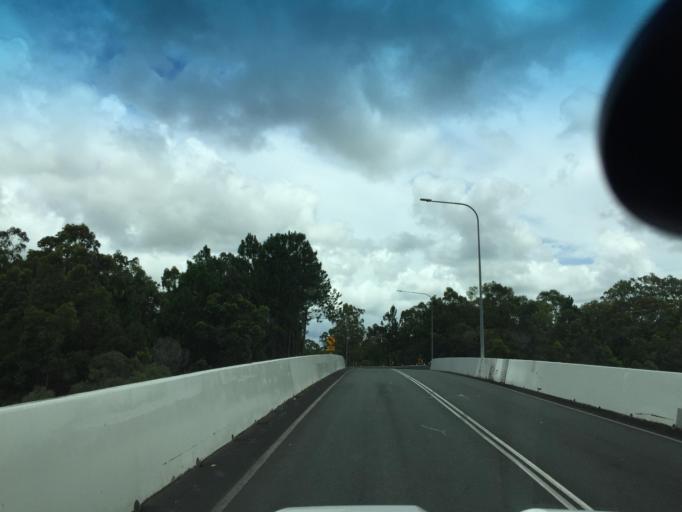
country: AU
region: Queensland
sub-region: Moreton Bay
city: Caboolture
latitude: -27.0607
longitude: 152.9089
